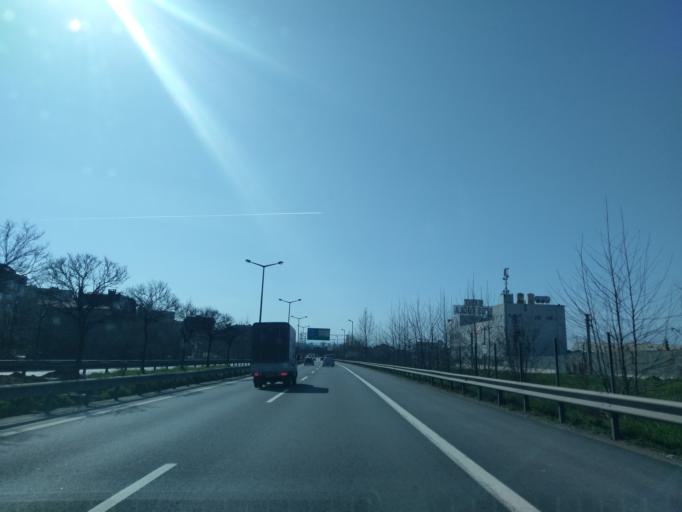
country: TR
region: Kocaeli
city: Darica
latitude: 40.8219
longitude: 29.3647
